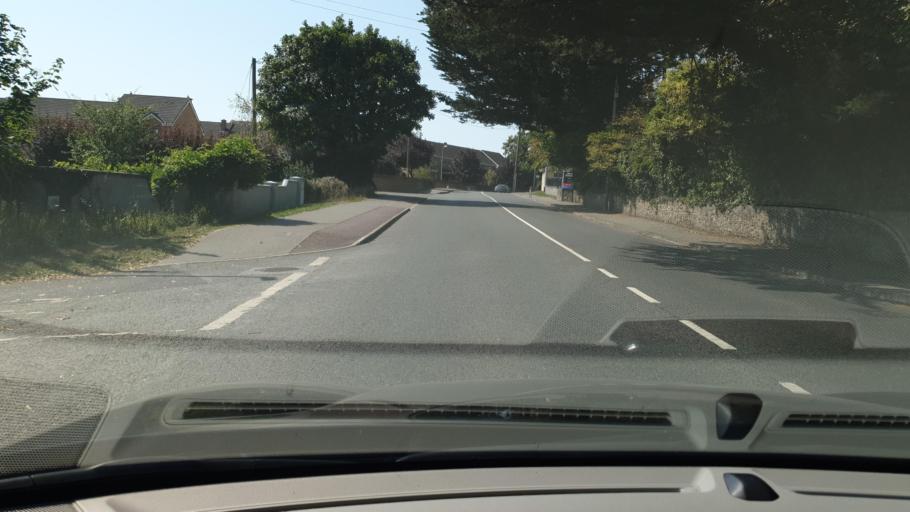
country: IE
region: Leinster
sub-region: An Mhi
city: Ratoath
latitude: 53.5055
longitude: -6.4547
